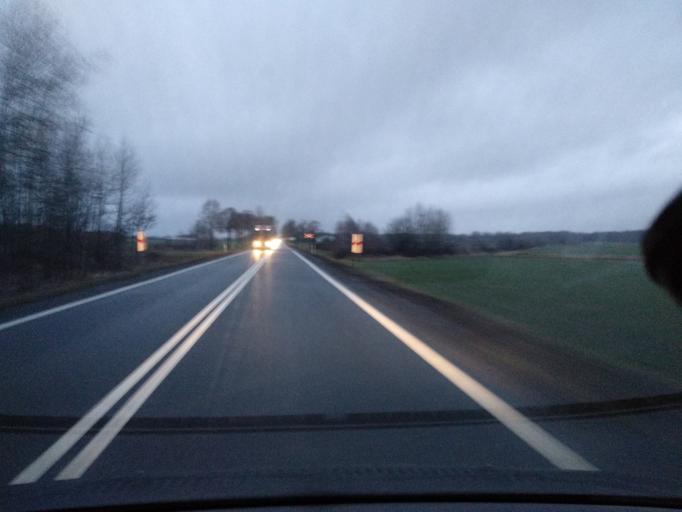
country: PL
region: Lower Silesian Voivodeship
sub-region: Powiat sredzki
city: Malczyce
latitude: 51.1808
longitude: 16.5264
